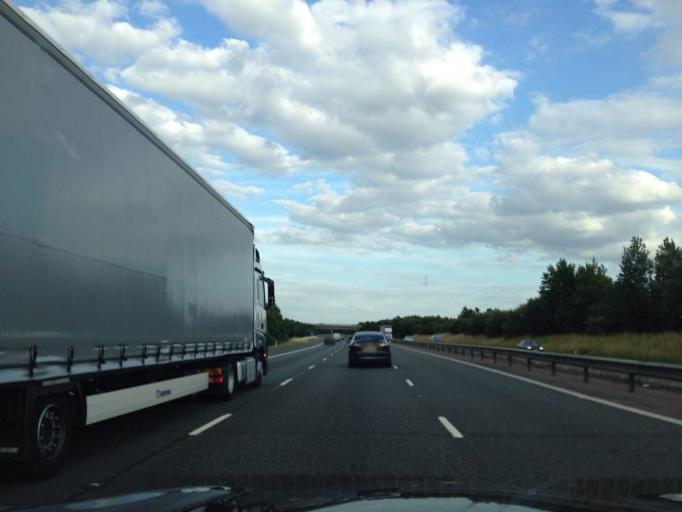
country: GB
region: England
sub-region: Oxfordshire
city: Bicester
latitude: 51.8463
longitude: -1.1620
